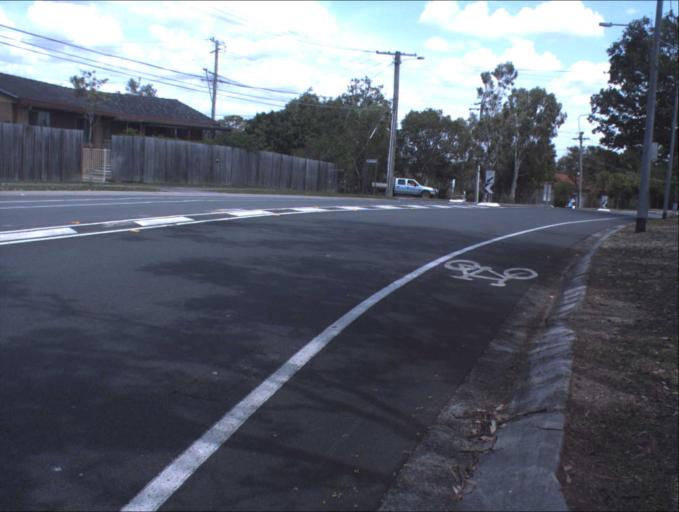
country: AU
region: Queensland
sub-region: Logan
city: Woodridge
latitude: -27.6271
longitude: 153.1001
